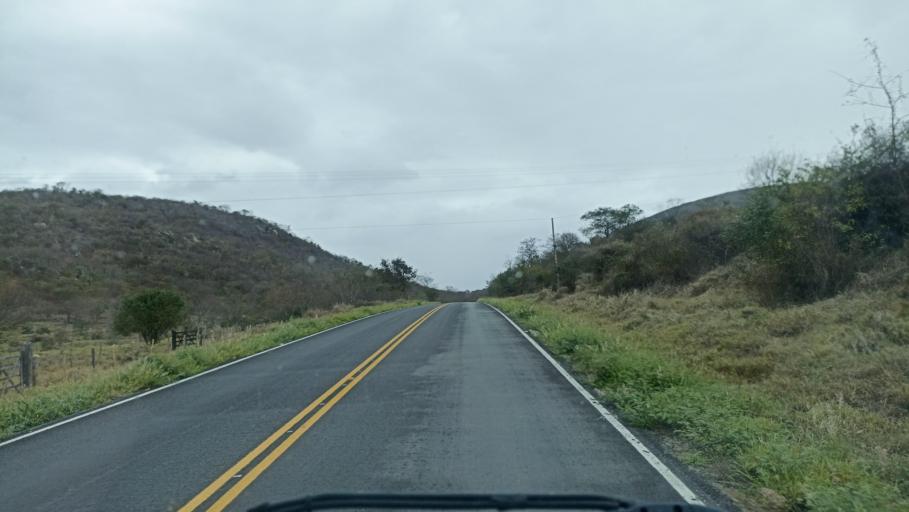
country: BR
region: Bahia
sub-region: Andarai
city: Vera Cruz
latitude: -13.0469
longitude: -40.7771
